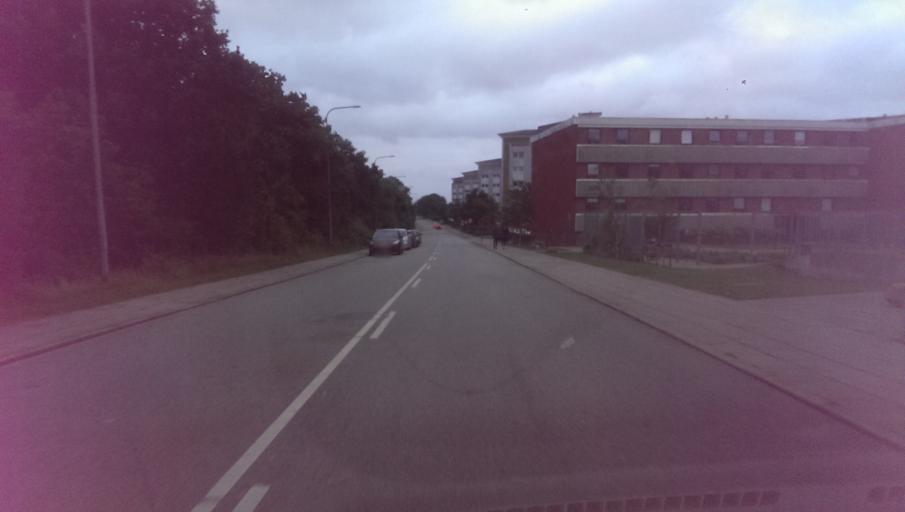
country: DK
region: South Denmark
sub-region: Esbjerg Kommune
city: Esbjerg
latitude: 55.4716
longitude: 8.4875
